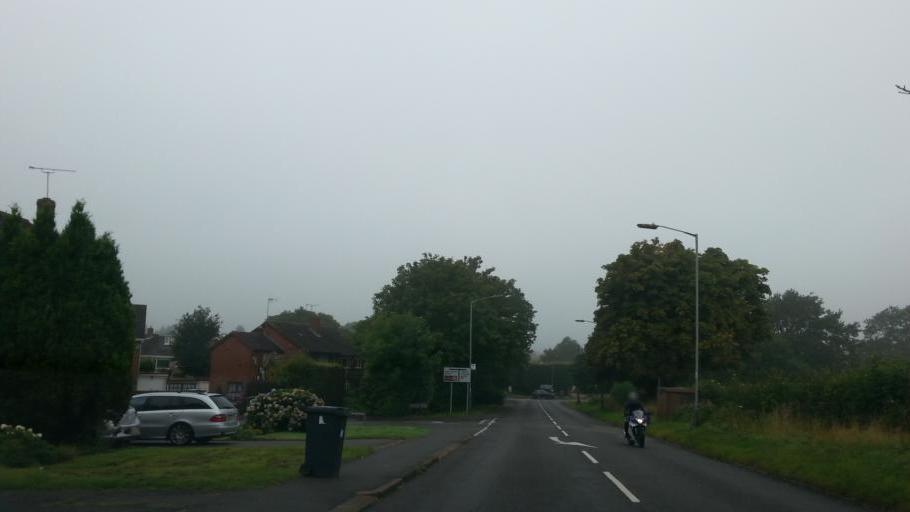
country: GB
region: England
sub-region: Warwickshire
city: Kenilworth
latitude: 52.3563
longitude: -1.5914
